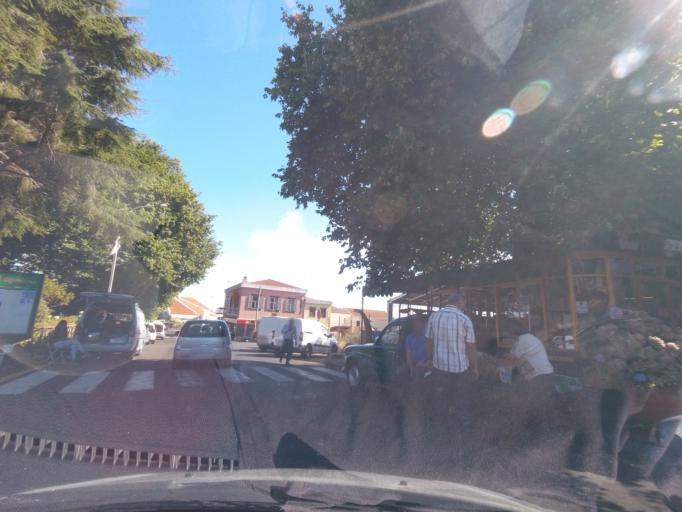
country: PT
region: Madeira
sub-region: Santa Cruz
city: Camacha
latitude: 32.6799
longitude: -16.8455
